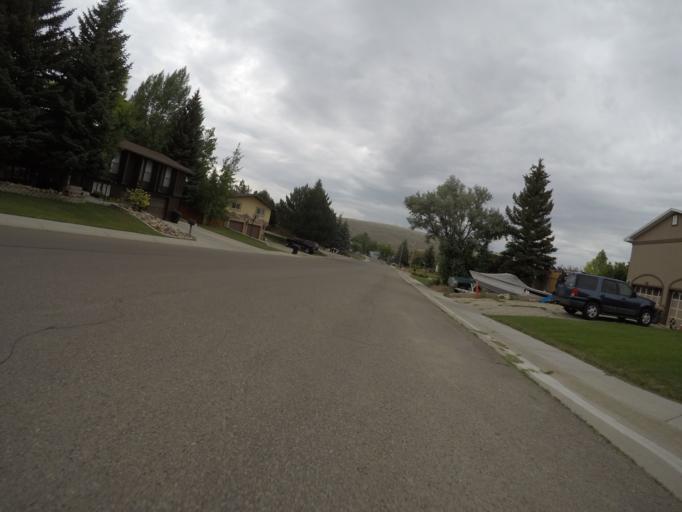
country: US
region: Wyoming
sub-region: Lincoln County
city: Kemmerer
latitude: 41.7906
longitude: -110.5464
